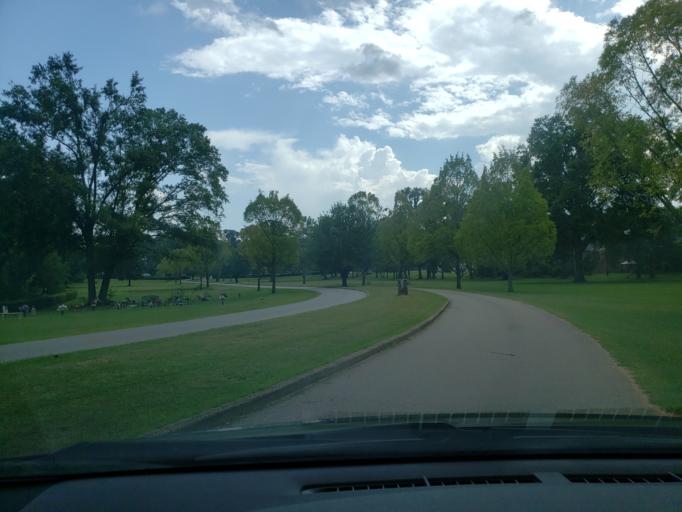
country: US
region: Georgia
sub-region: Dougherty County
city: Albany
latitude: 31.5999
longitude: -84.1967
